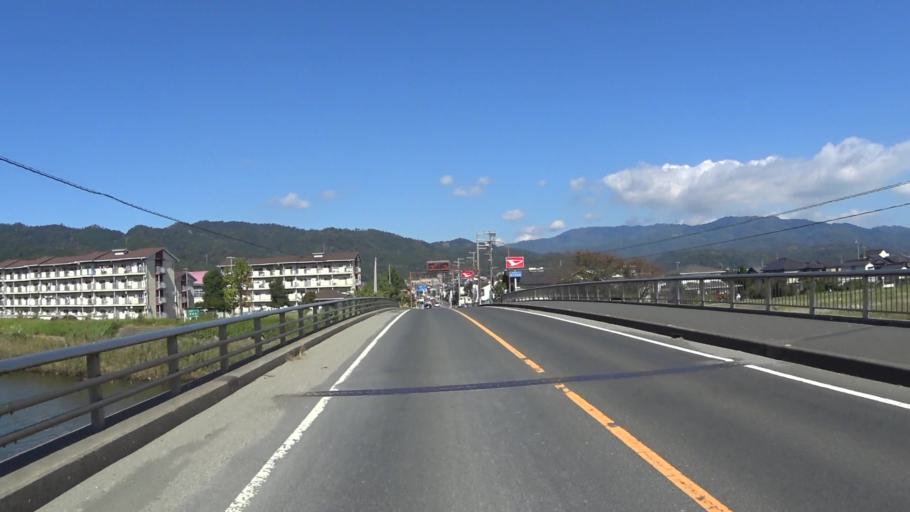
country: JP
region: Kyoto
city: Miyazu
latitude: 35.5589
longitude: 135.1534
